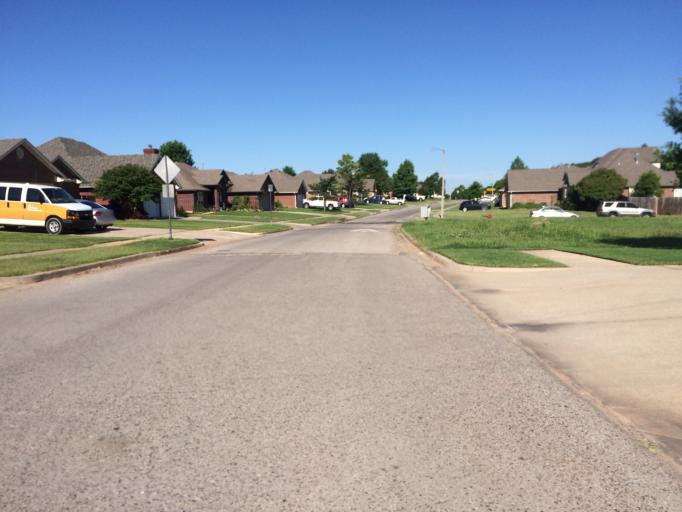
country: US
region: Oklahoma
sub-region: Cleveland County
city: Norman
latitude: 35.2389
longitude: -97.4338
